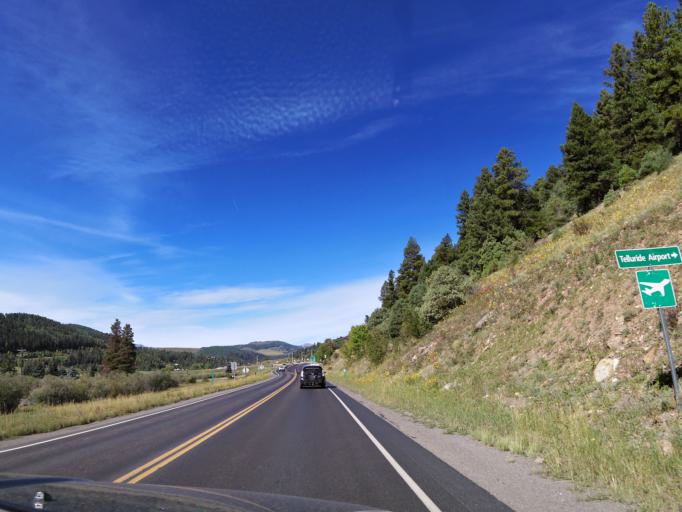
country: US
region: Colorado
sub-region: San Miguel County
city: Mountain Village
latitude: 37.9511
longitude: -107.8658
